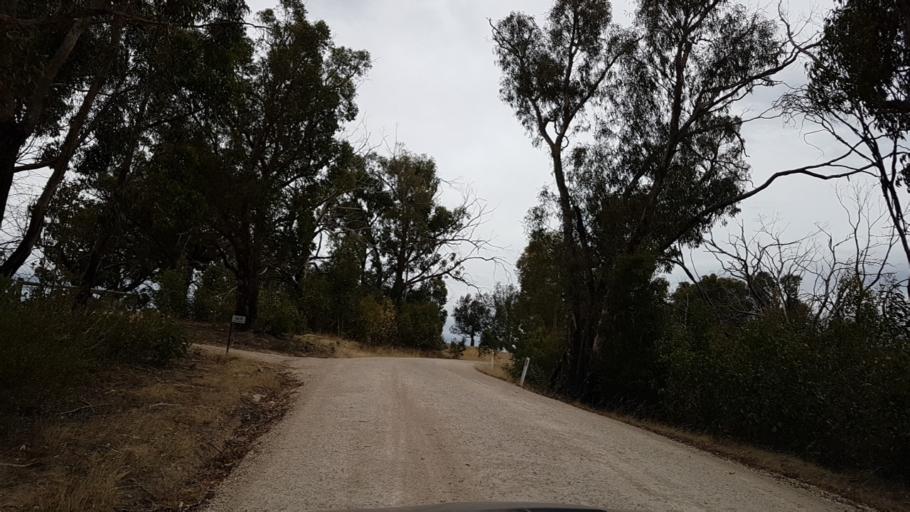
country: AU
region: South Australia
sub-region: Tea Tree Gully
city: Golden Grove
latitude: -34.7779
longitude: 138.8128
